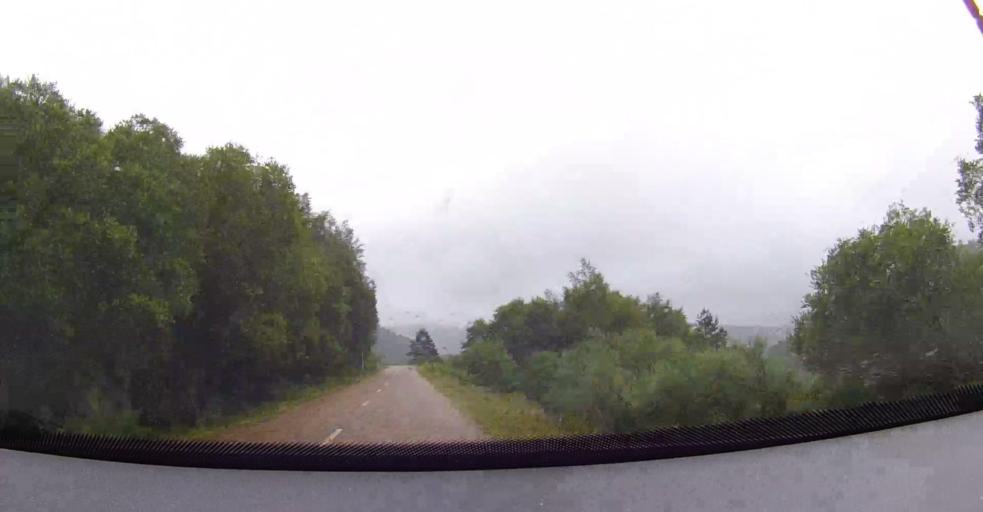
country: ES
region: Castille and Leon
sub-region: Provincia de Leon
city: Puebla de Lillo
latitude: 43.0761
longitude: -5.2672
